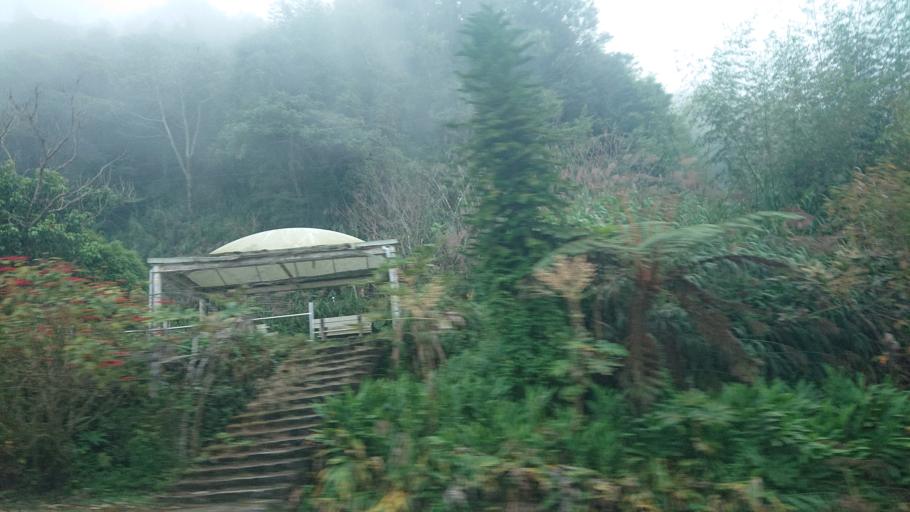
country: TW
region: Taiwan
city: Lugu
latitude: 23.5152
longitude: 120.7032
